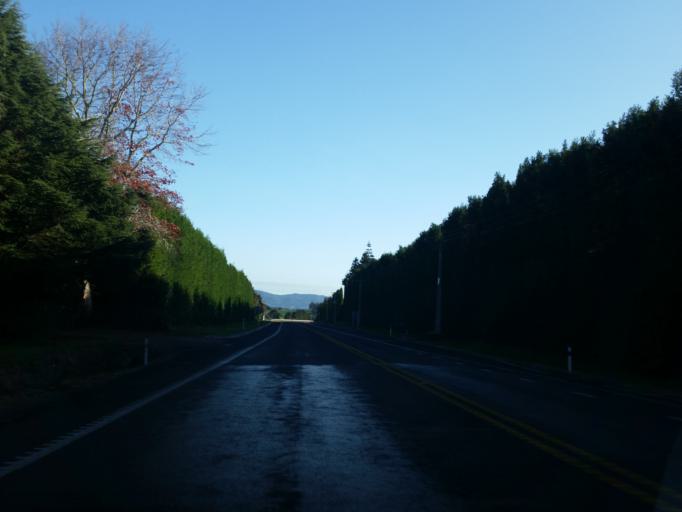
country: NZ
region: Bay of Plenty
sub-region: Western Bay of Plenty District
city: Katikati
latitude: -37.6250
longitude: 175.9547
